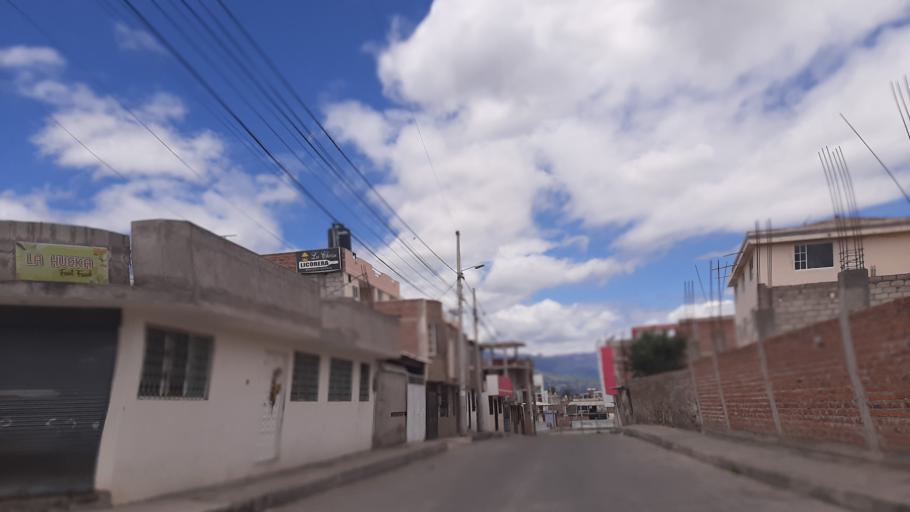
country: EC
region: Chimborazo
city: Riobamba
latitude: -1.6562
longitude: -78.6411
